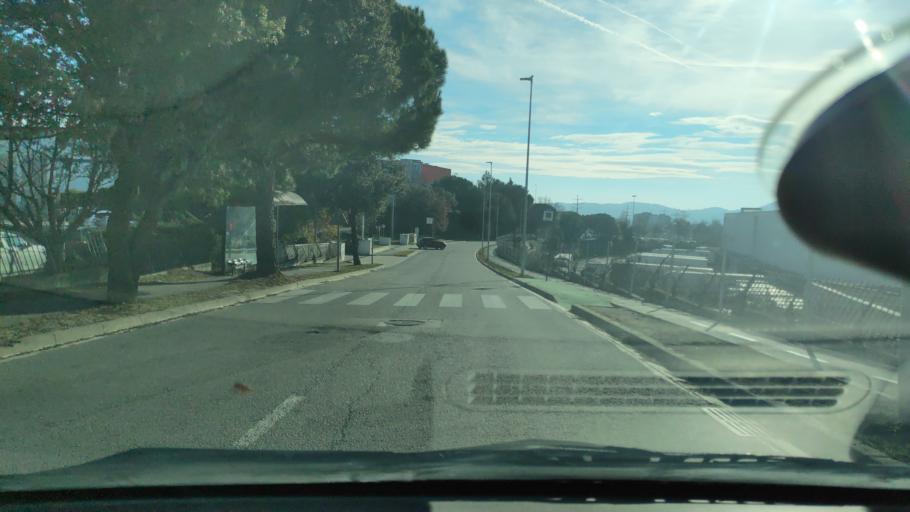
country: ES
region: Catalonia
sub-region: Provincia de Barcelona
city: Rubi
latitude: 41.4895
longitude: 2.0518
